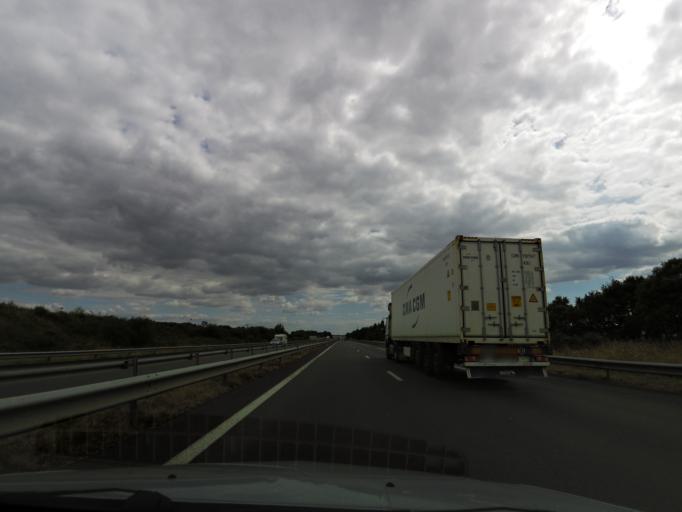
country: FR
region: Pays de la Loire
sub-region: Departement de la Loire-Atlantique
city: Le Bignon
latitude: 47.1245
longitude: -1.5009
